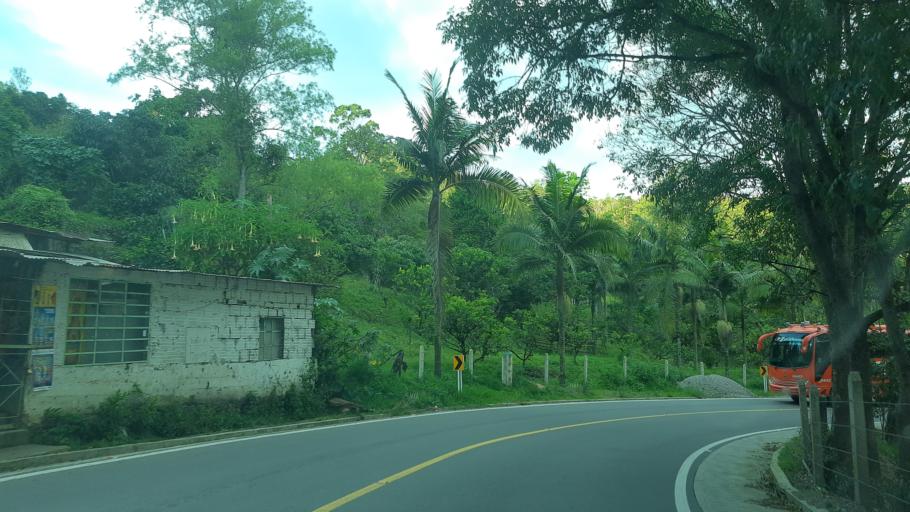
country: CO
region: Boyaca
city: Somondoco
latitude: 5.0078
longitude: -73.4455
